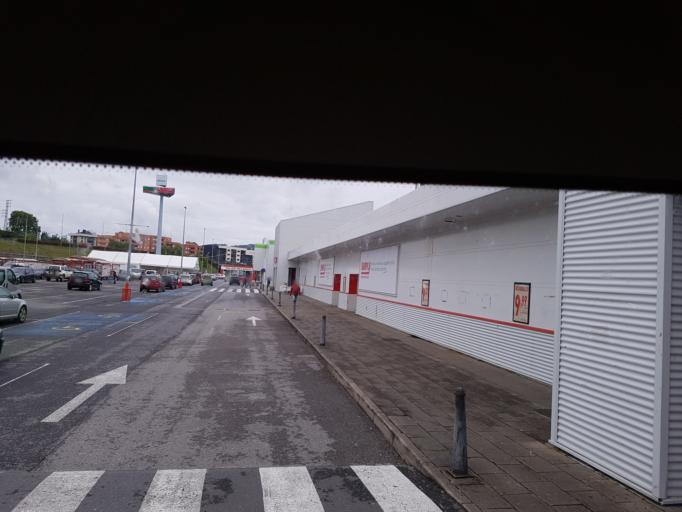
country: ES
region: Basque Country
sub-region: Bizkaia
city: Abadino
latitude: 43.1634
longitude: -2.6193
